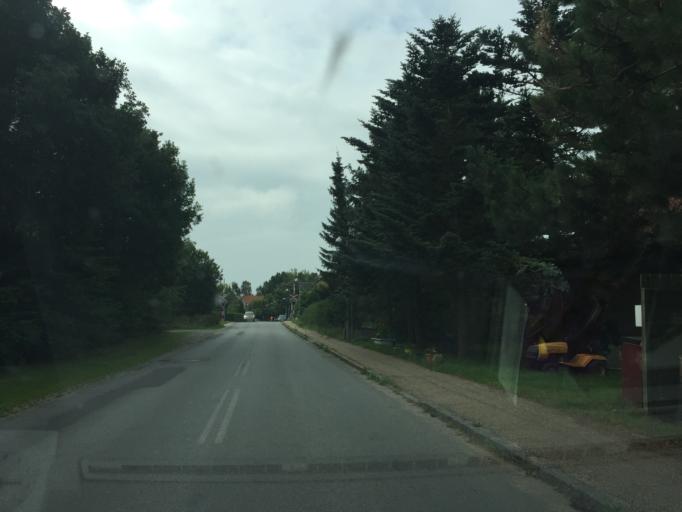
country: DK
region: Capital Region
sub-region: Helsingor Kommune
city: Hornbaek
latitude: 56.0779
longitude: 12.4843
